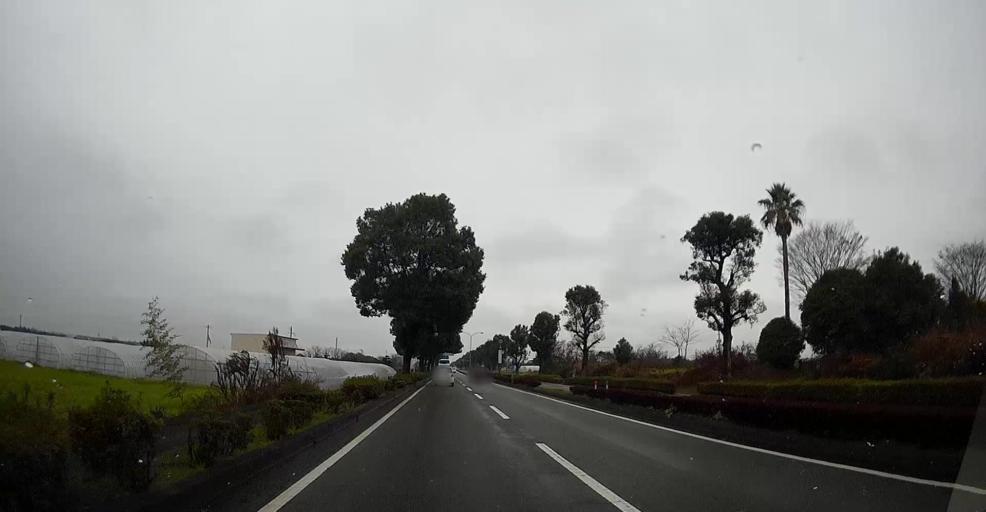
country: JP
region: Kumamoto
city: Ozu
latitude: 32.8080
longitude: 130.8146
